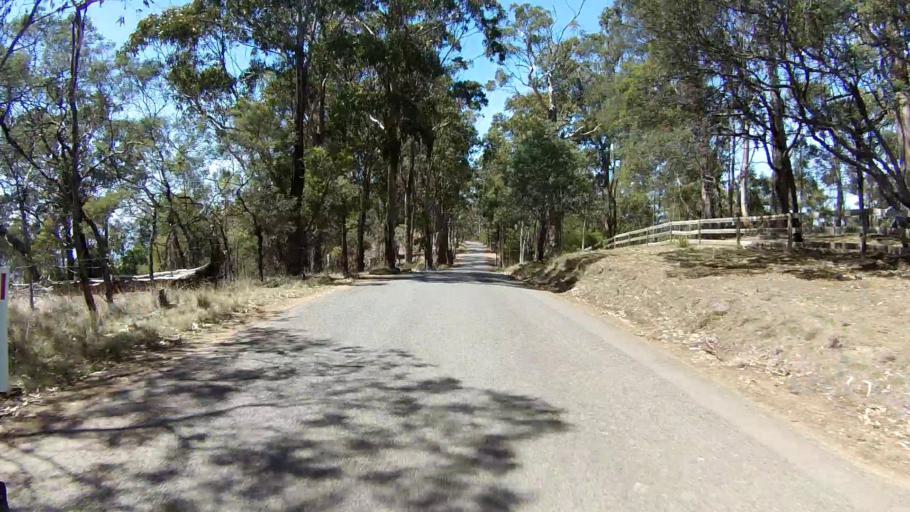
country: AU
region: Tasmania
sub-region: Clarence
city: Cambridge
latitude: -42.8586
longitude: 147.4455
